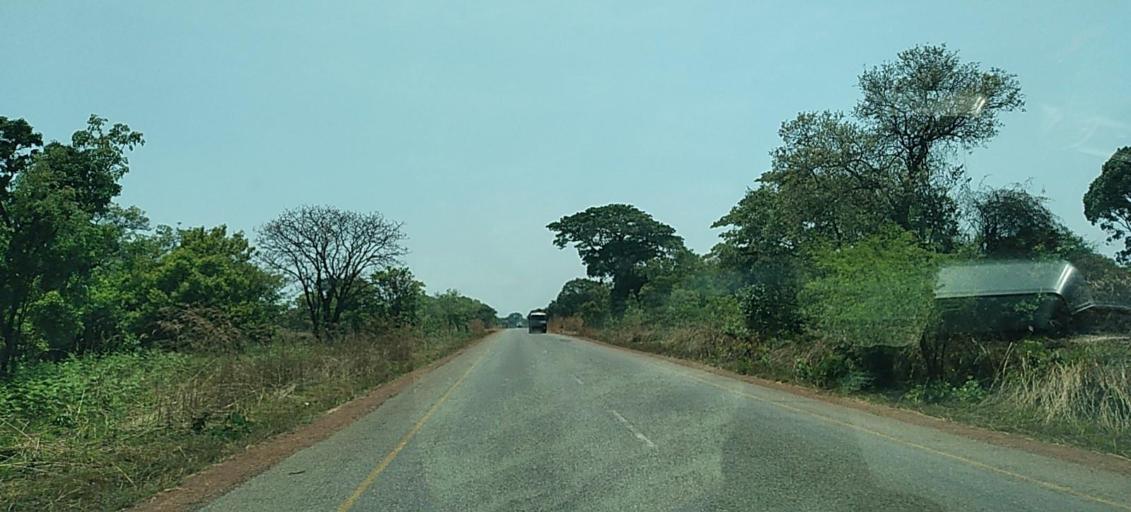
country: ZM
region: North-Western
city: Solwezi
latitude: -12.3842
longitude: 26.1793
